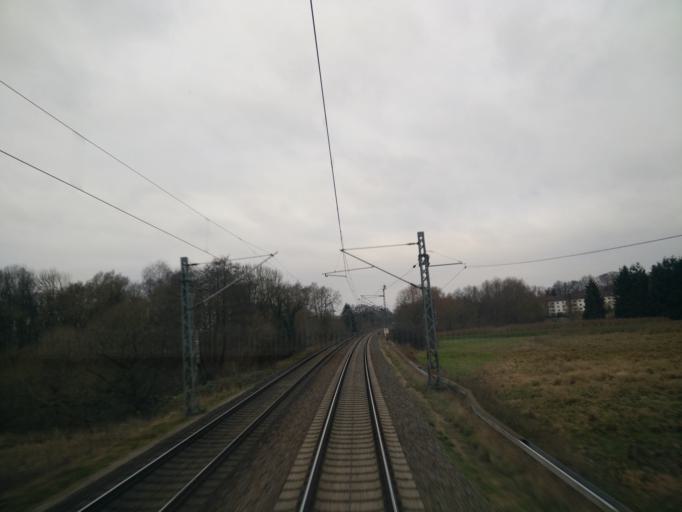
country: DE
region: Mecklenburg-Vorpommern
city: Grabow
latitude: 53.2785
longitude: 11.5719
